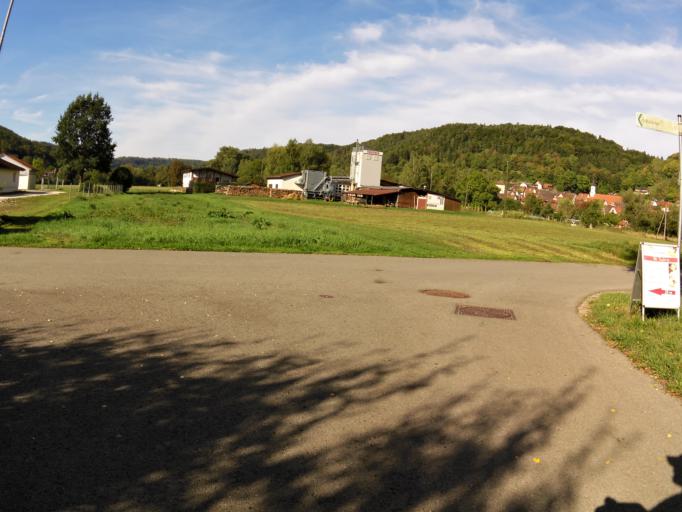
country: DE
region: Baden-Wuerttemberg
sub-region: Tuebingen Region
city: Hirrlingen
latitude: 48.4506
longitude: 8.8594
